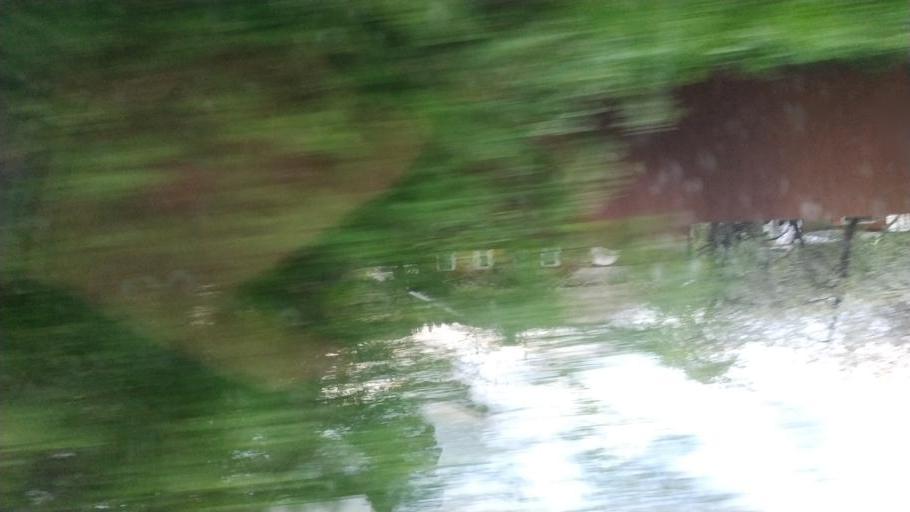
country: RU
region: Moskovskaya
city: Kashira
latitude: 54.8446
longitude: 38.1709
